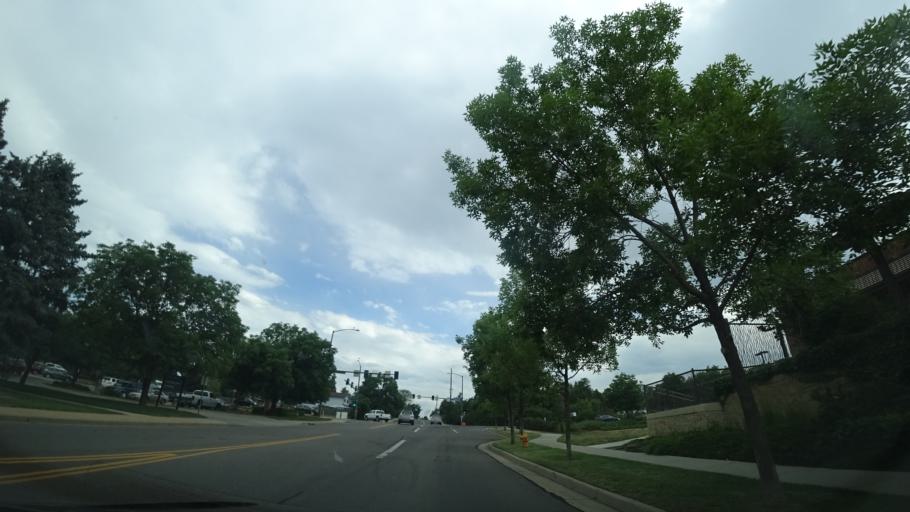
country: US
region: Colorado
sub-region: Jefferson County
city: Lakewood
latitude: 39.7117
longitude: -105.0910
